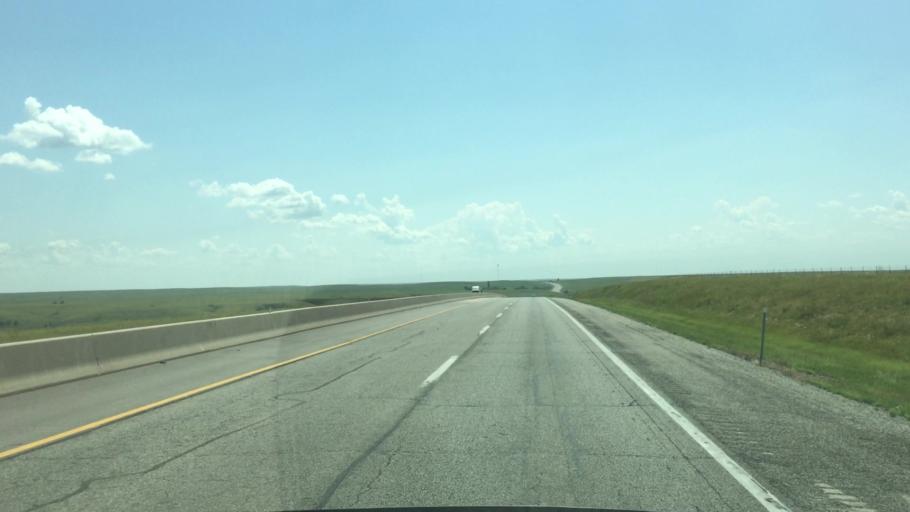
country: US
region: Kansas
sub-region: Chase County
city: Cottonwood Falls
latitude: 38.1872
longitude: -96.4553
